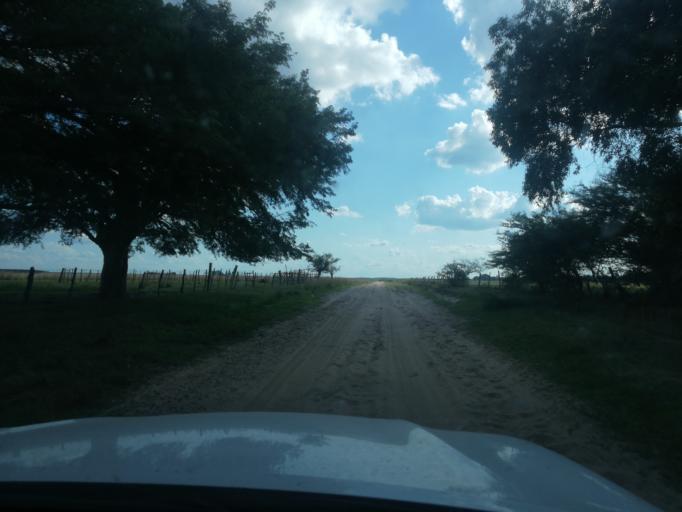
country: AR
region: Corrientes
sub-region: Departamento de San Miguel
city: San Miguel
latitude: -27.9922
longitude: -57.5709
